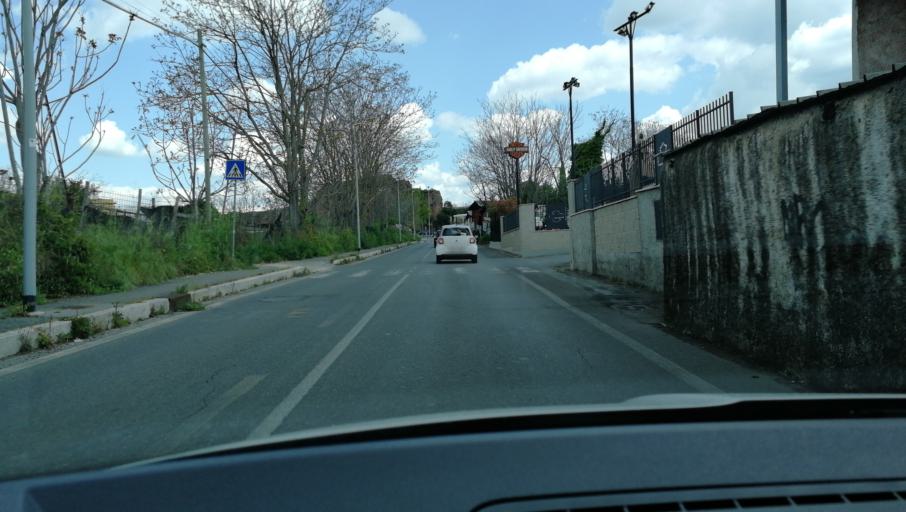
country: IT
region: Latium
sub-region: Citta metropolitana di Roma Capitale
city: Rome
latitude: 41.8633
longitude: 12.5407
